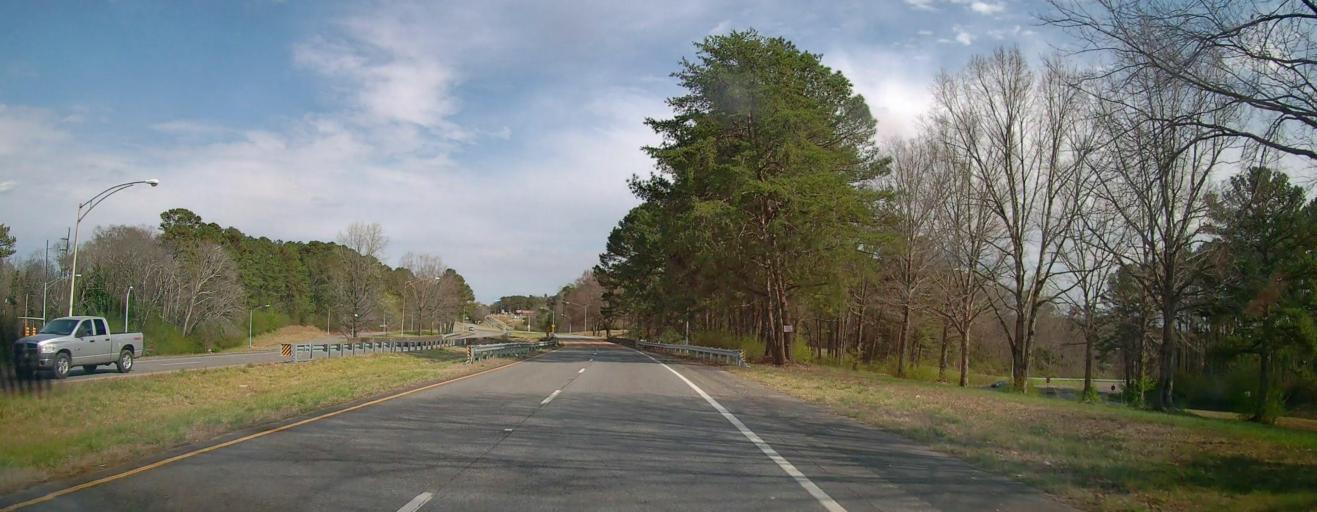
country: US
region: Alabama
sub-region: Jefferson County
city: Adamsville
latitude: 33.5859
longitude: -86.9329
